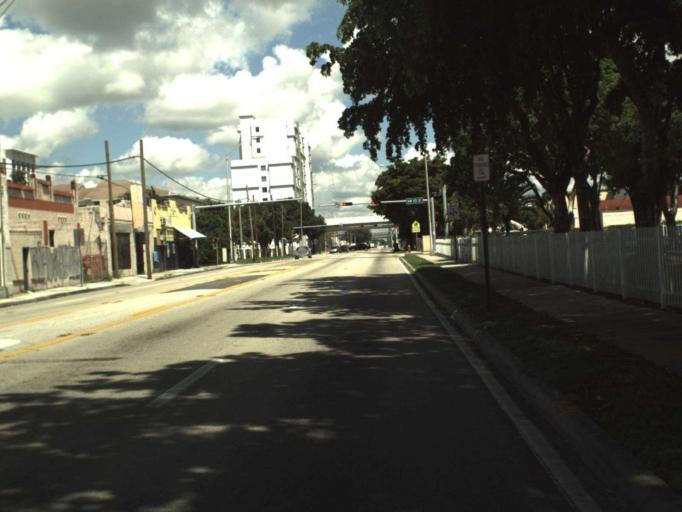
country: US
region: Florida
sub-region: Miami-Dade County
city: Miami
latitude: 25.7826
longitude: -80.2067
